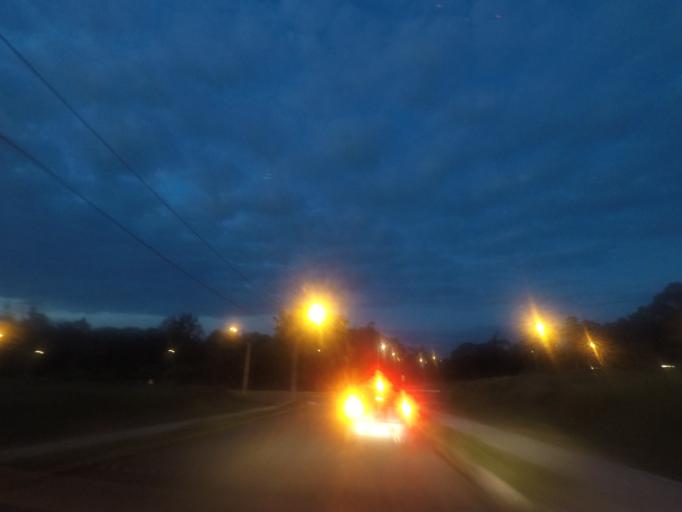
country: BR
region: Parana
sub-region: Pinhais
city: Pinhais
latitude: -25.3834
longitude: -49.2052
